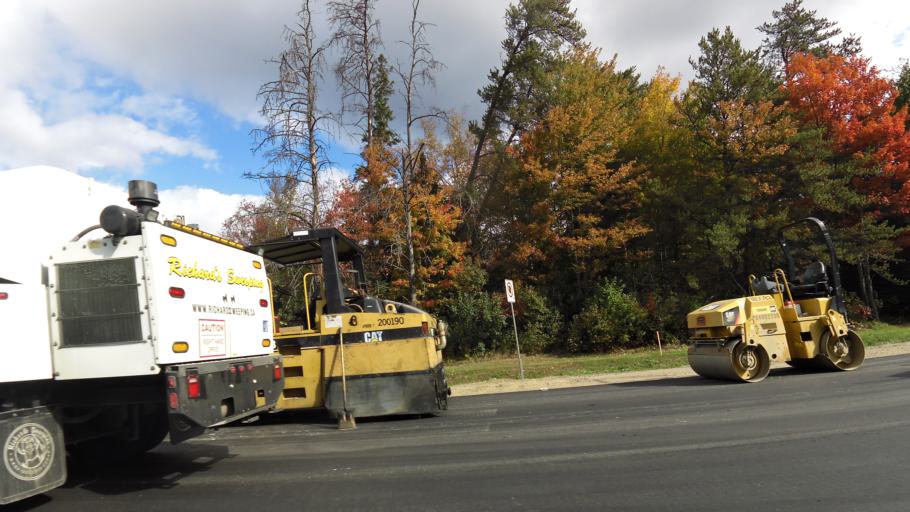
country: CA
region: Ontario
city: Deep River
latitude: 46.0999
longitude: -77.4986
